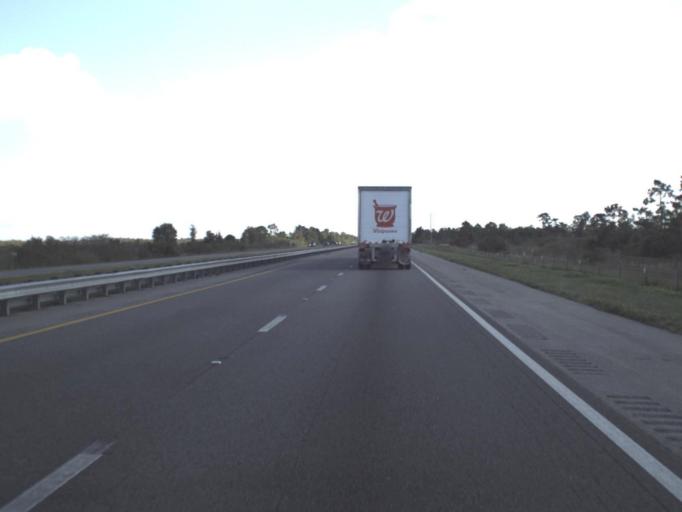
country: US
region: Florida
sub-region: Indian River County
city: Fellsmere
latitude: 27.7732
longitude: -80.9633
